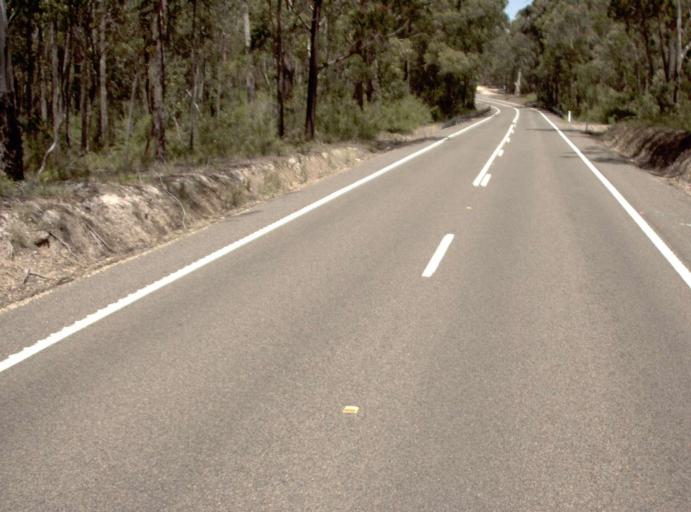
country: AU
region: Victoria
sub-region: East Gippsland
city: Lakes Entrance
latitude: -37.7628
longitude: 148.0594
